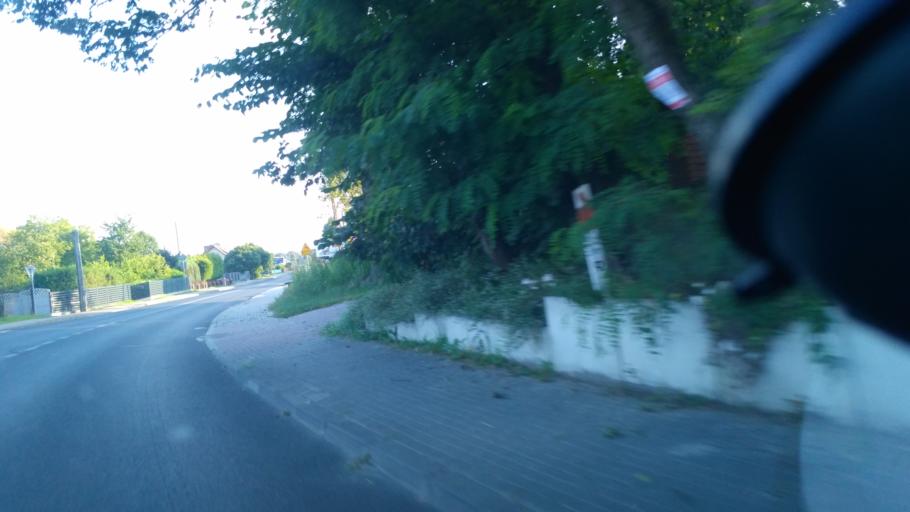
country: PL
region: Subcarpathian Voivodeship
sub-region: Powiat lezajski
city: Stare Miasto
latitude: 50.2827
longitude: 22.4305
